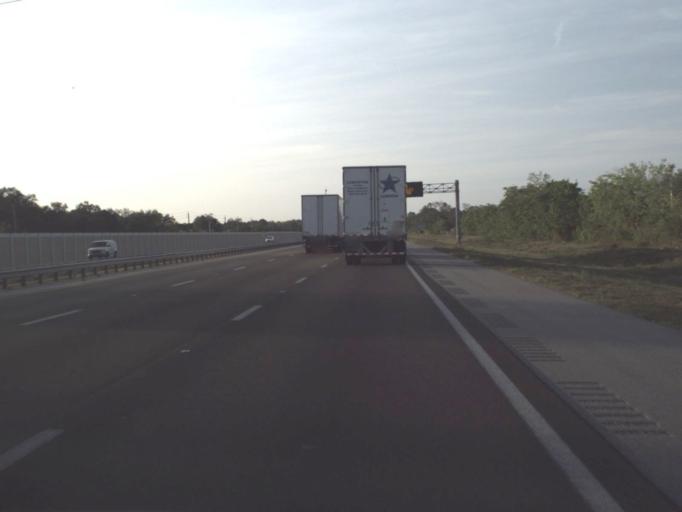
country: US
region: Florida
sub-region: Brevard County
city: Mims
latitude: 28.6514
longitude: -80.8635
